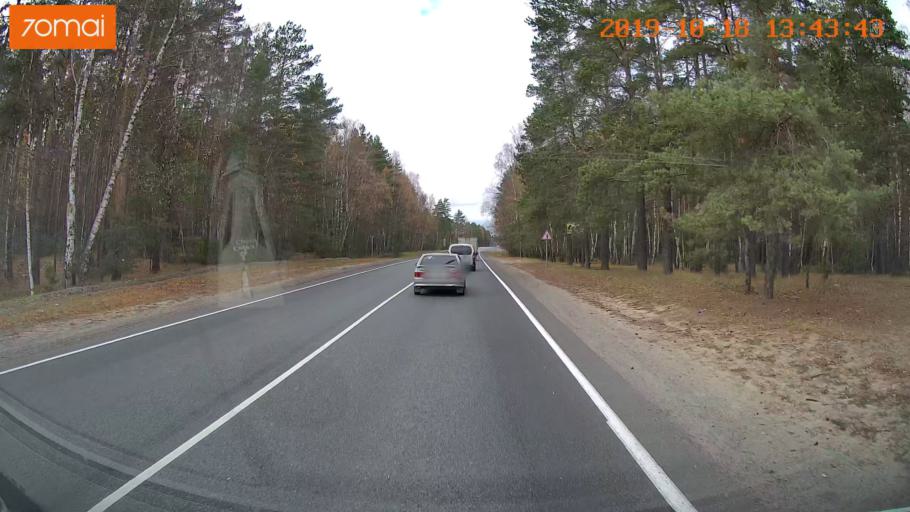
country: RU
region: Rjazan
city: Solotcha
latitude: 54.9323
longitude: 39.9730
